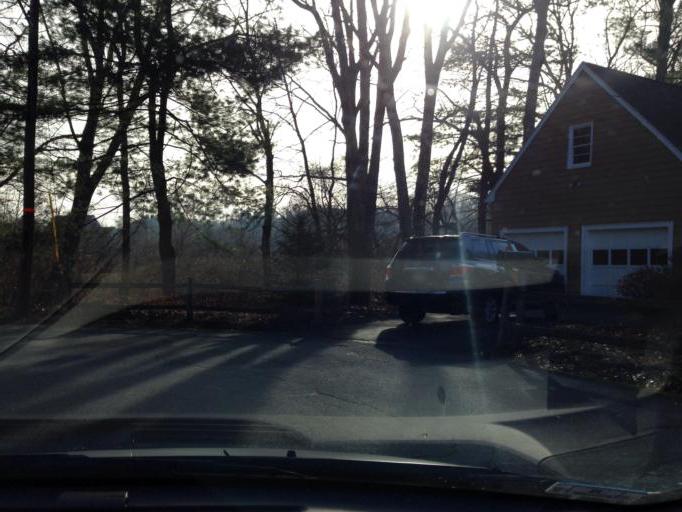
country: US
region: Massachusetts
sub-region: Middlesex County
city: Bedford
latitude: 42.4958
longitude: -71.3058
